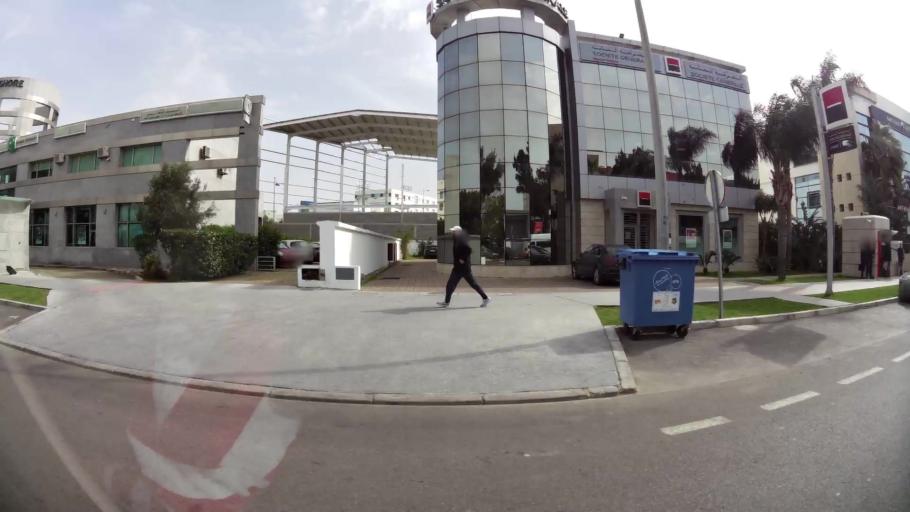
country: MA
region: Tanger-Tetouan
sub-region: Tanger-Assilah
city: Boukhalef
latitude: 35.7153
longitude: -5.9070
